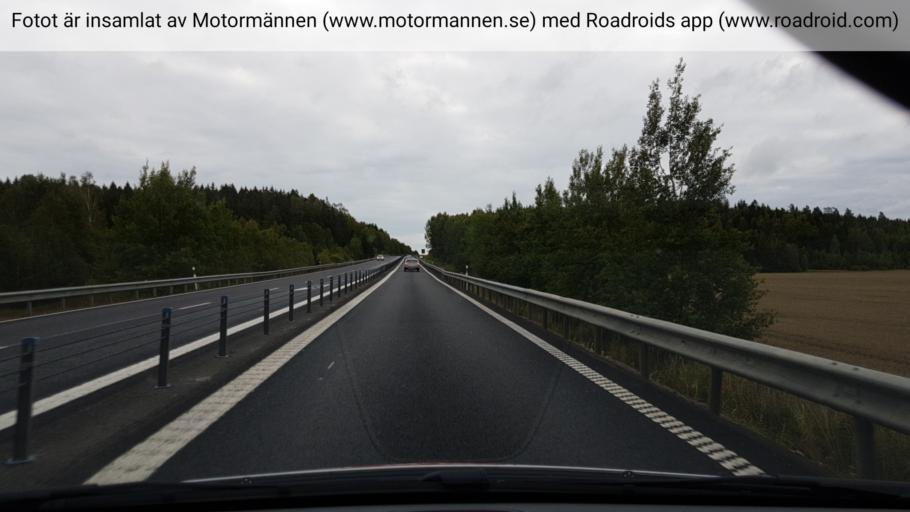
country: SE
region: Vaermland
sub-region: Karlstads Kommun
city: Skattkarr
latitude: 59.4013
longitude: 13.7886
